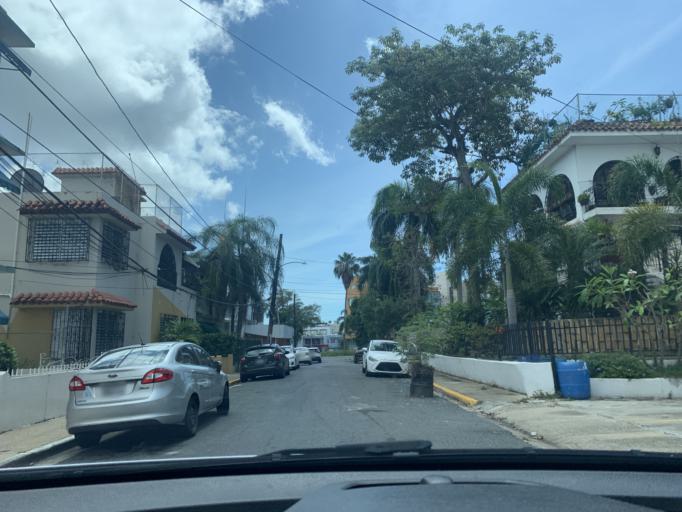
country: PR
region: Trujillo Alto
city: Trujillo Alto
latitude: 18.4021
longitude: -66.0556
